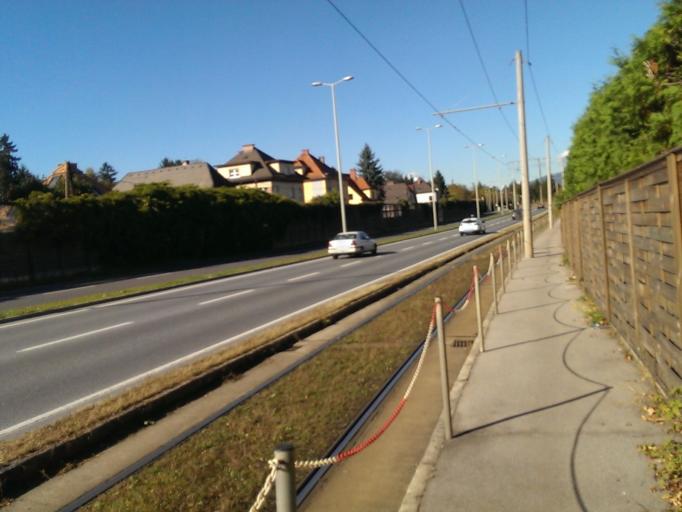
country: AT
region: Styria
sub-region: Politischer Bezirk Graz-Umgebung
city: Feldkirchen bei Graz
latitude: 47.0389
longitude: 15.4304
